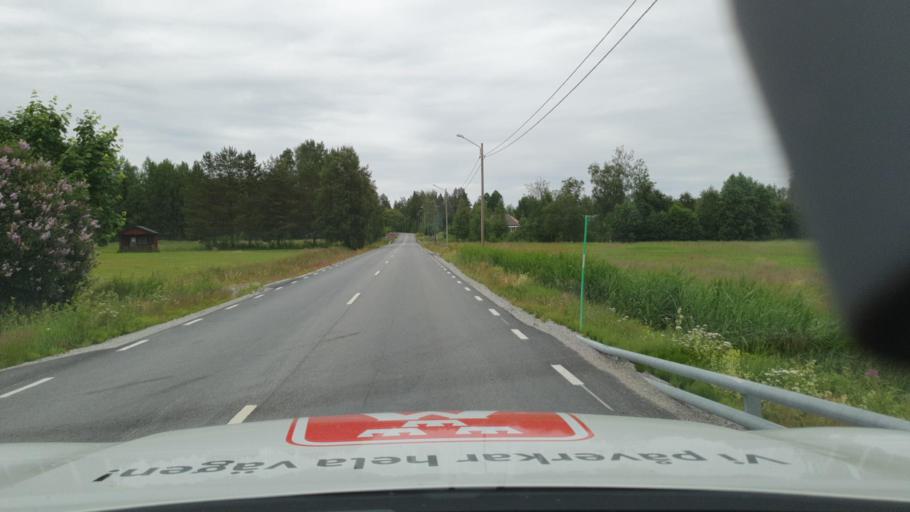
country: SE
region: Vaesterbotten
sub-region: Nordmalings Kommun
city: Nordmaling
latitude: 63.4998
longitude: 19.3242
